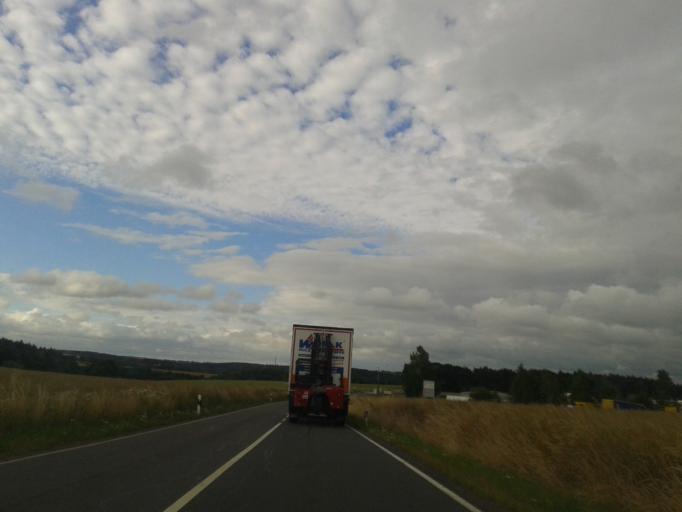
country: DE
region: Saxony
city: Reinsberg
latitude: 51.0314
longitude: 13.3464
